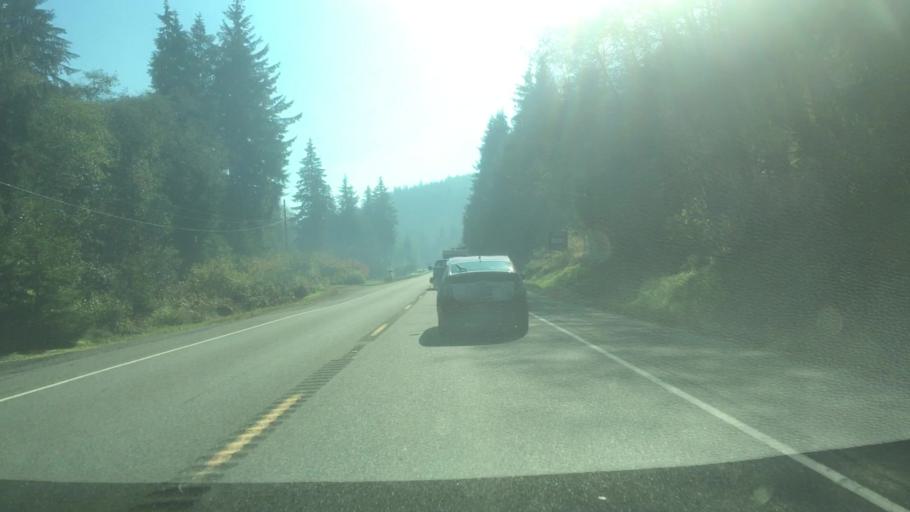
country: US
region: Washington
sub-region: Grays Harbor County
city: Central Park
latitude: 46.9227
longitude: -123.7176
